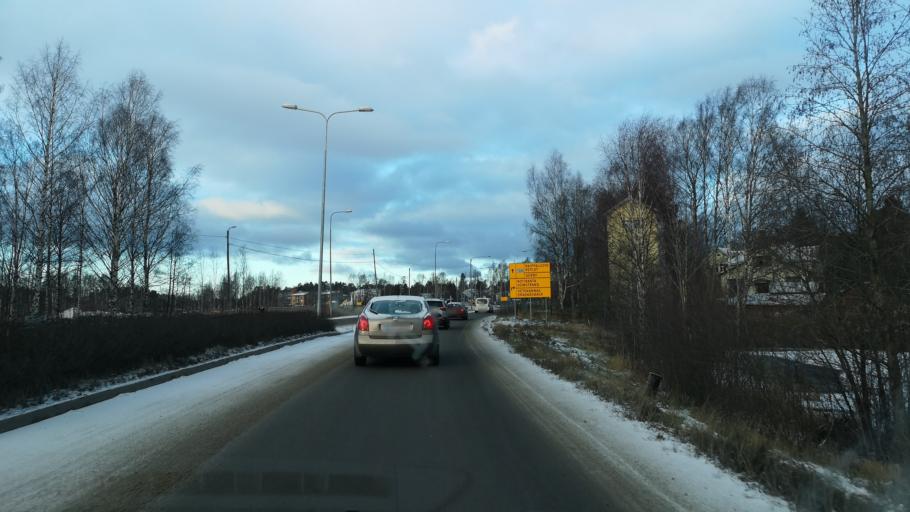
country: FI
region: Ostrobothnia
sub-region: Vaasa
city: Vaasa
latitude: 63.1115
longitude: 21.6192
